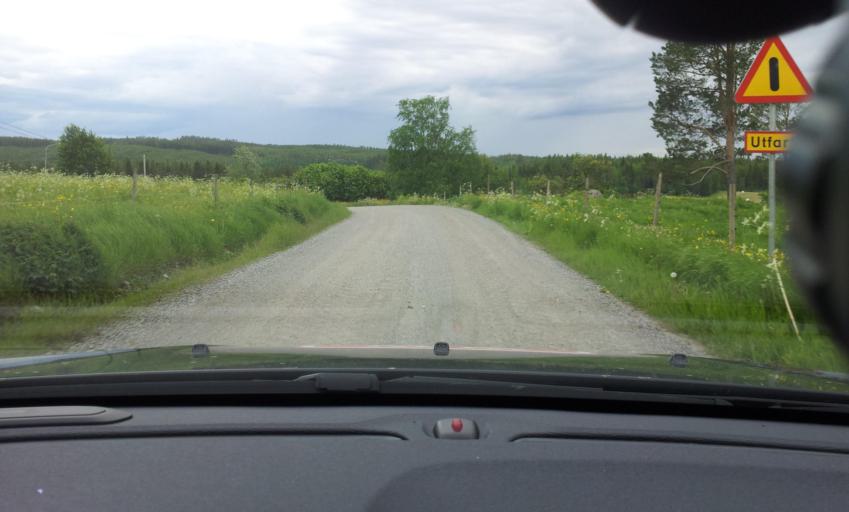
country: SE
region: Jaemtland
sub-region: OEstersunds Kommun
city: Brunflo
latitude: 62.9756
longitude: 14.6837
